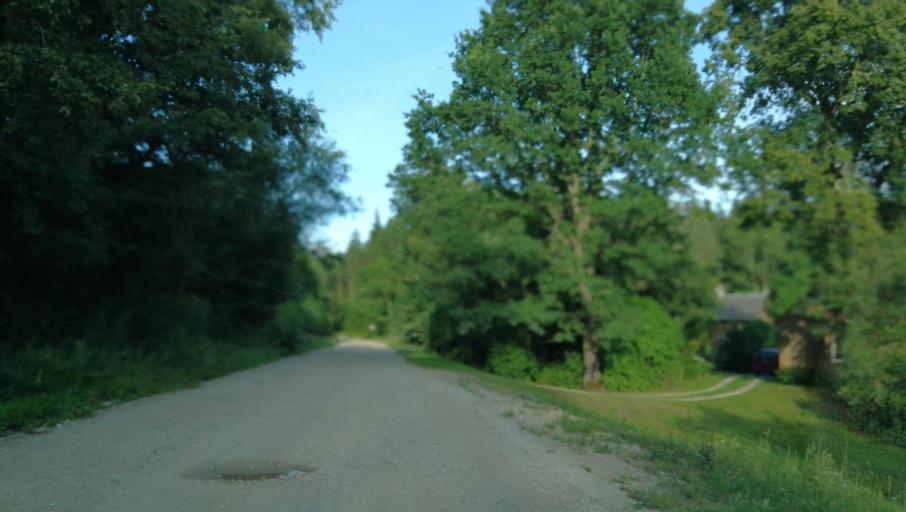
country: LV
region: Cesu Rajons
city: Cesis
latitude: 57.3500
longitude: 25.1951
